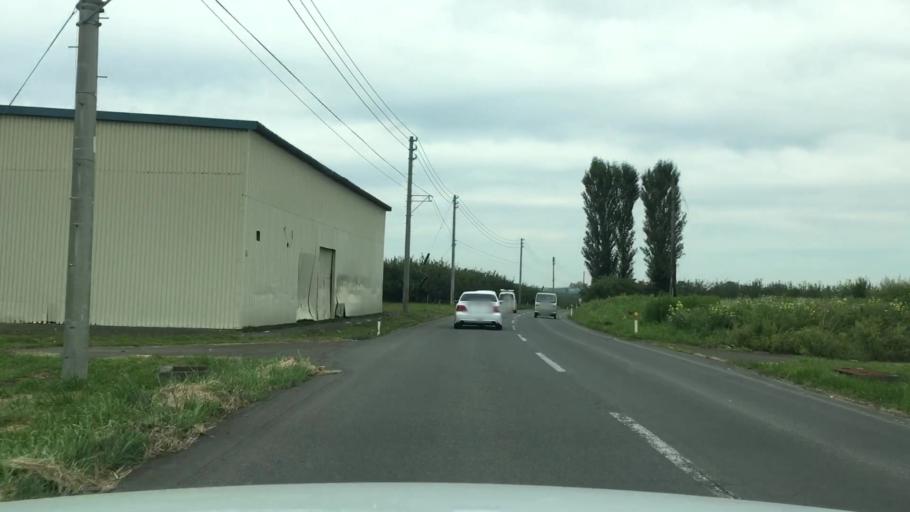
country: JP
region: Aomori
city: Hirosaki
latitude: 40.6462
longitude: 140.4241
